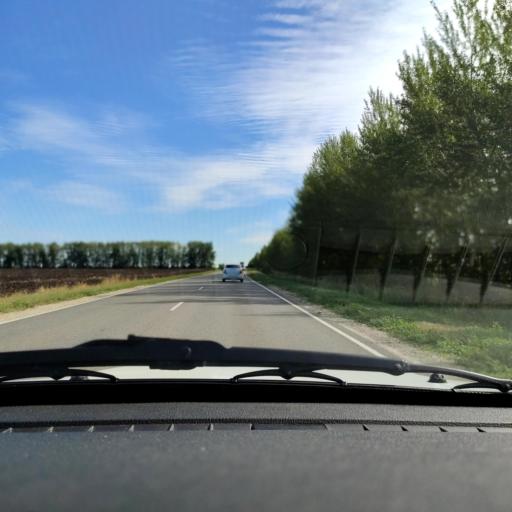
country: RU
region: Voronezj
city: Volya
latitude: 51.7236
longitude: 39.5477
